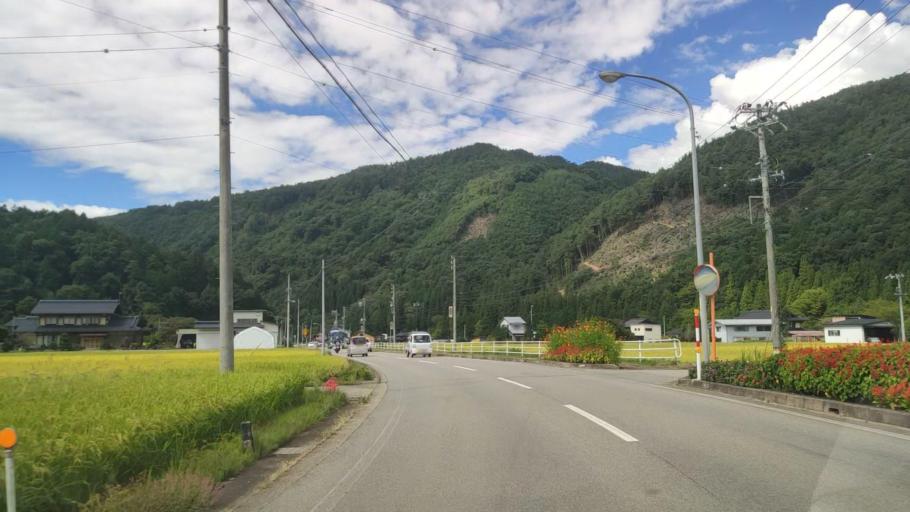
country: JP
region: Gifu
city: Takayama
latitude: 36.1792
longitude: 137.2822
